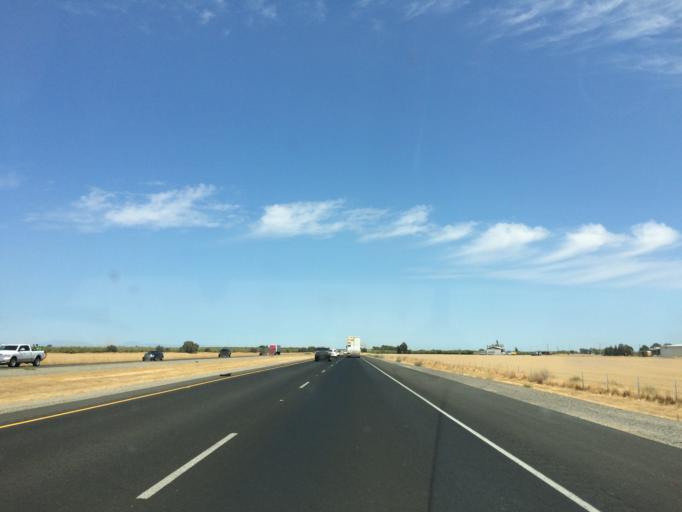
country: US
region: California
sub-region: Colusa County
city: Arbuckle
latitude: 38.9561
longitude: -122.0192
